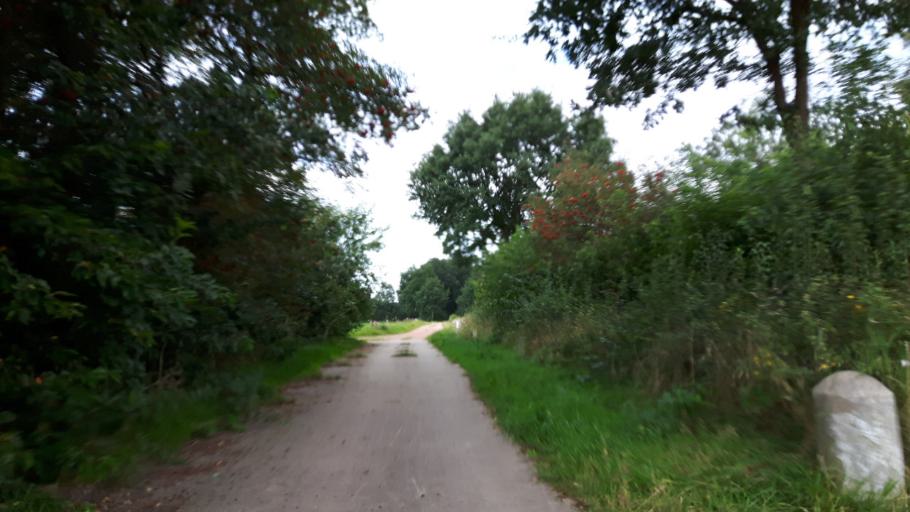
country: NL
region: Groningen
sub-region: Gemeente Leek
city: Leek
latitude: 53.0830
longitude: 6.3233
